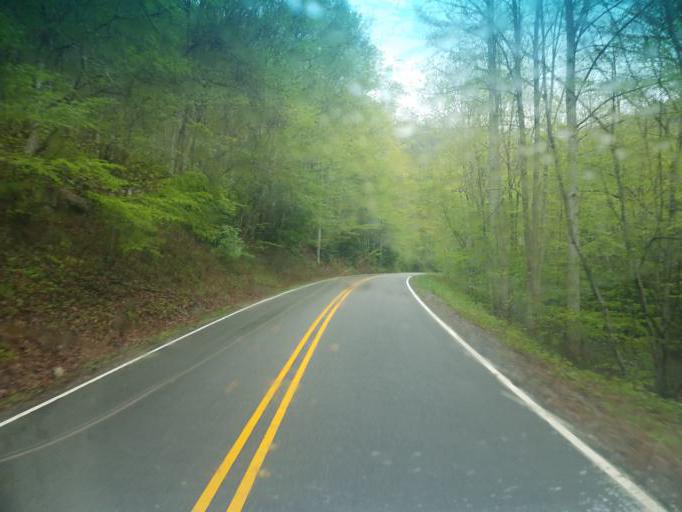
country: US
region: Virginia
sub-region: Washington County
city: Glade Spring
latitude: 36.6297
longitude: -81.7560
